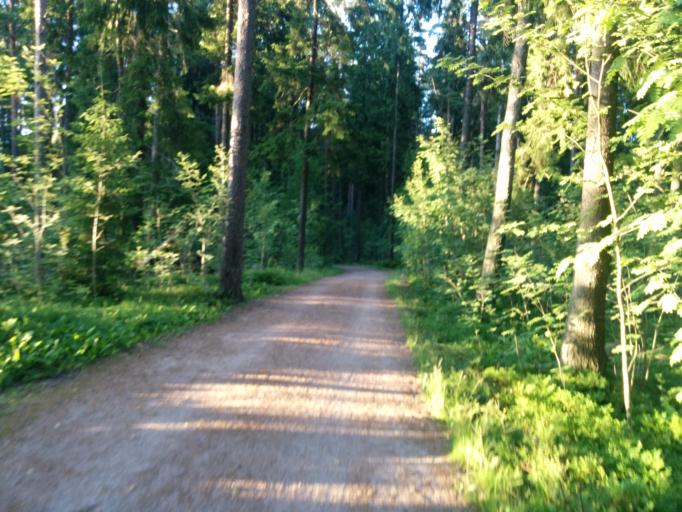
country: FI
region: Uusimaa
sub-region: Helsinki
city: Helsinki
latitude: 60.2167
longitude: 24.9164
